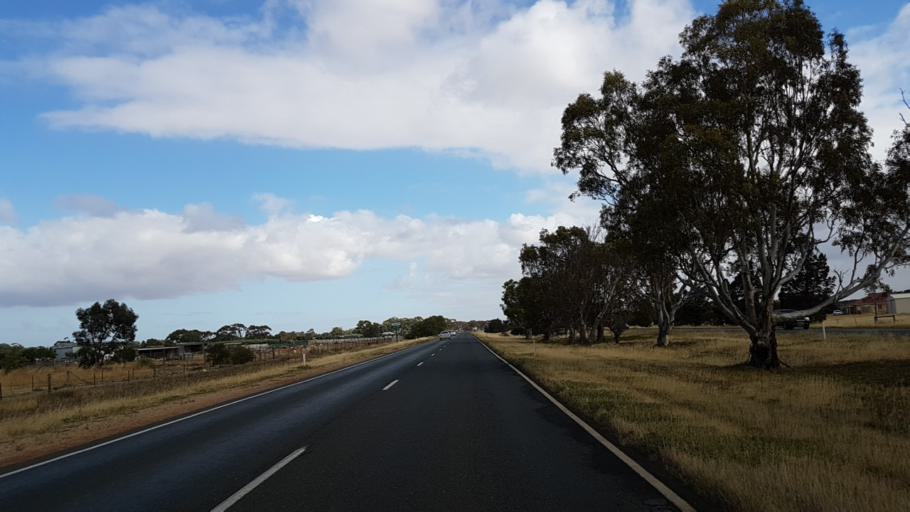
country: AU
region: South Australia
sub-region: Mallala
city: Two Wells
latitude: -34.6193
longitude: 138.5205
